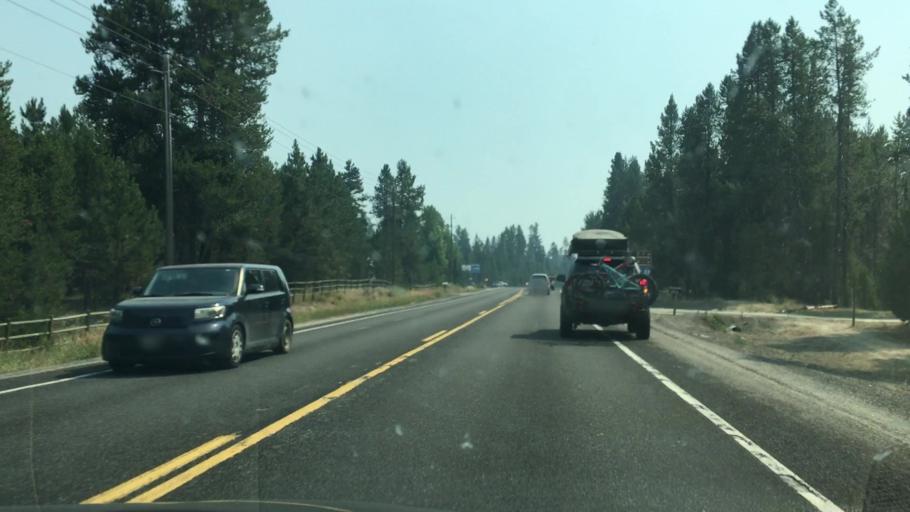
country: US
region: Idaho
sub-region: Valley County
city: Cascade
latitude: 44.4094
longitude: -115.9998
